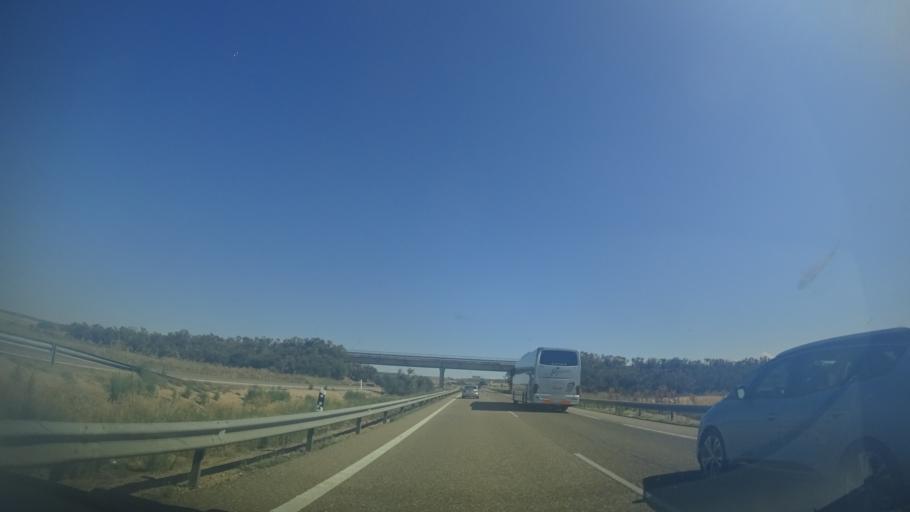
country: ES
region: Castille and Leon
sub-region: Provincia de Valladolid
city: Villardefrades
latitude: 41.7362
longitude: -5.2660
